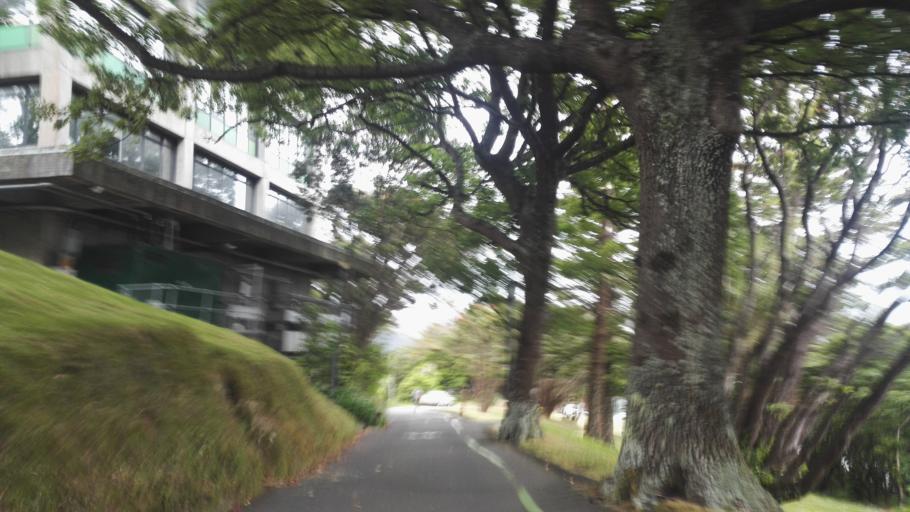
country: NZ
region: Wellington
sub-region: Wellington City
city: Kelburn
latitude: -41.2838
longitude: 174.7689
